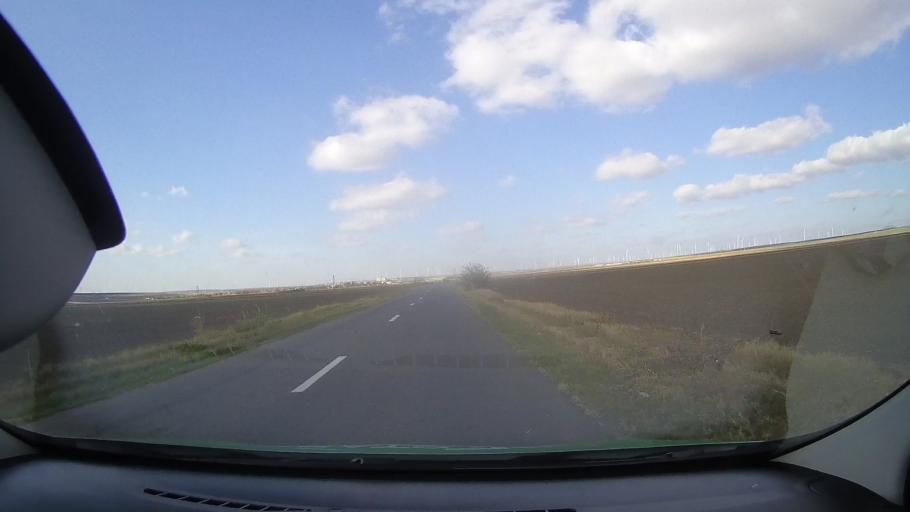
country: RO
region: Constanta
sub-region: Comuna Cogealac
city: Tariverde
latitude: 44.5522
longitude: 28.6246
